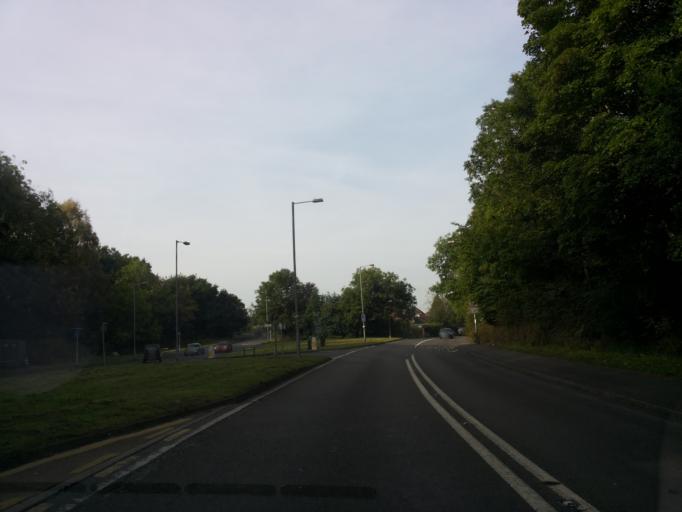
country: GB
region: England
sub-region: Worcestershire
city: Stourport-on-Severn
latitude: 52.3333
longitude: -2.2879
